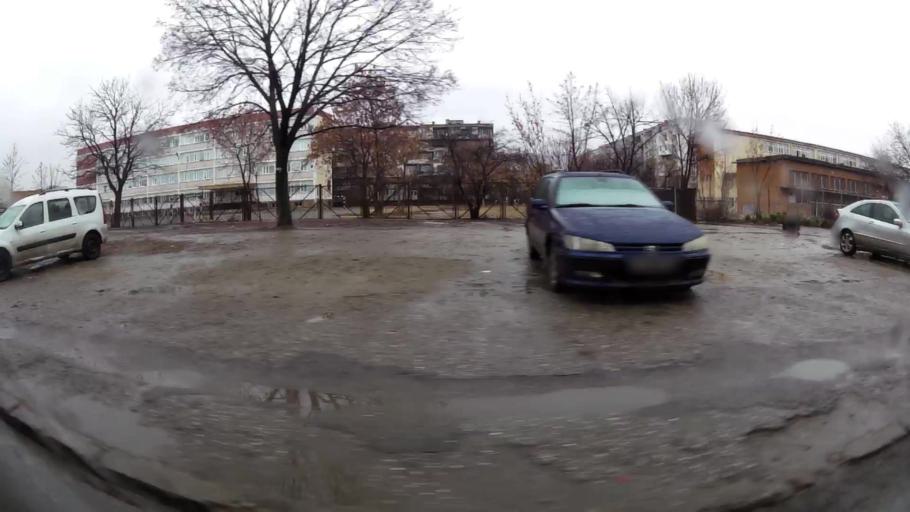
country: BG
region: Sofia-Capital
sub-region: Stolichna Obshtina
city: Sofia
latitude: 42.6652
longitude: 23.3963
